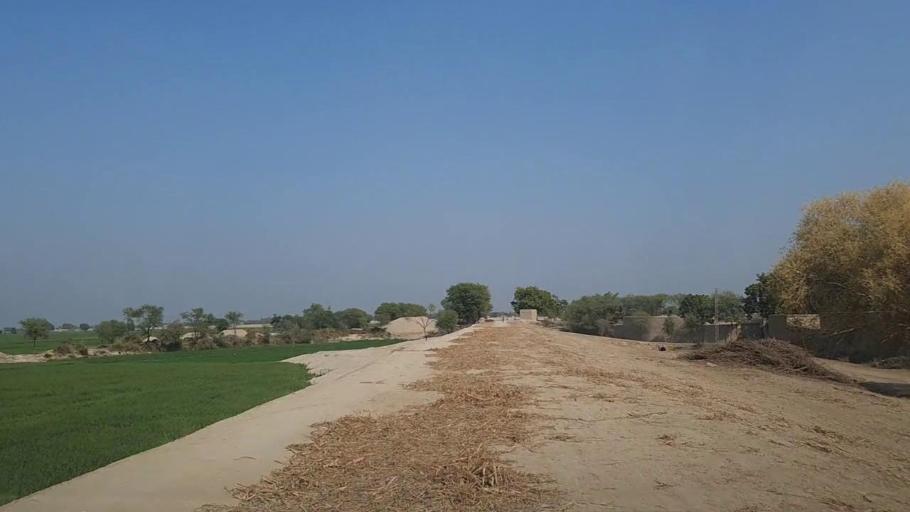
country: PK
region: Sindh
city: Naushahro Firoz
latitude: 26.8587
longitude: 67.9663
